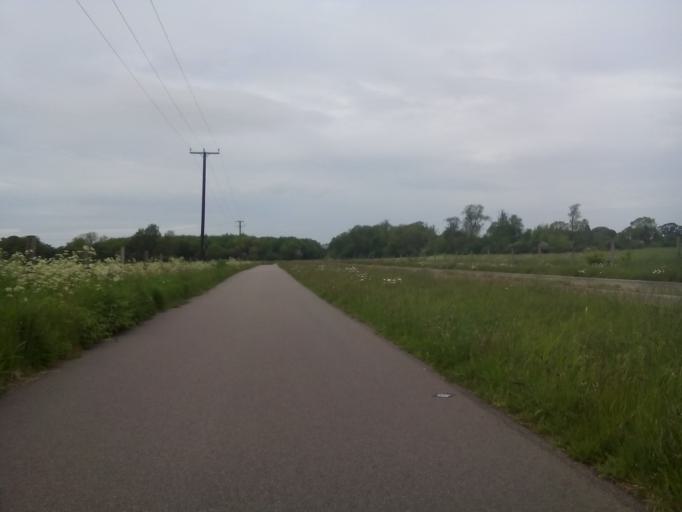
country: GB
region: England
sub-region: Cambridgeshire
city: Histon
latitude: 52.2597
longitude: 0.0831
